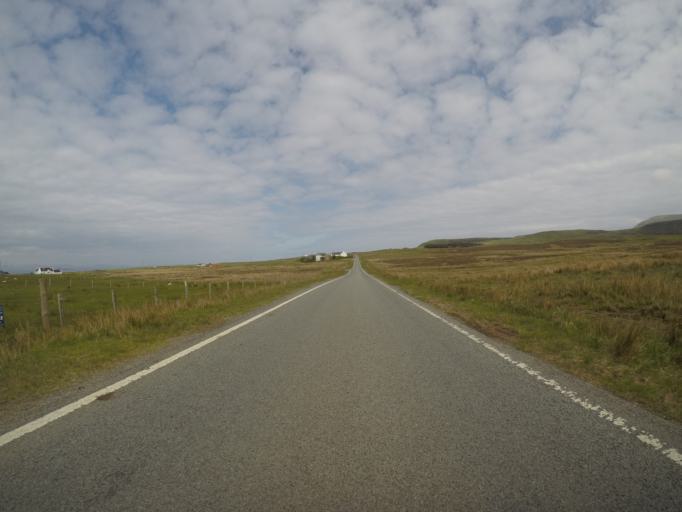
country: GB
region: Scotland
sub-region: Highland
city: Portree
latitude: 57.6551
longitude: -6.3779
